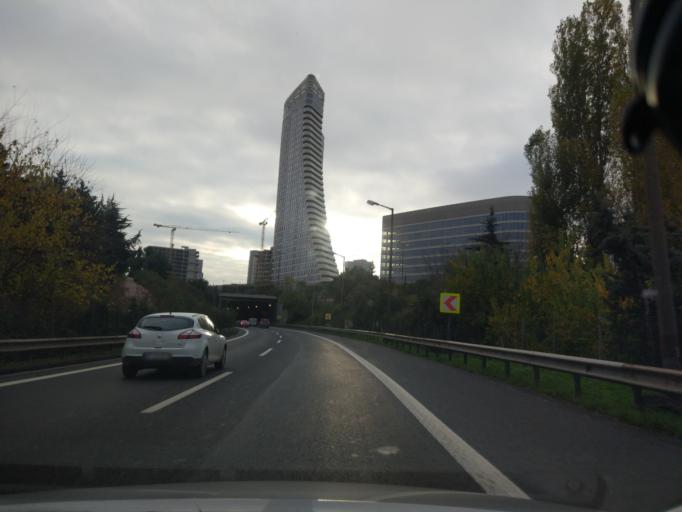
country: TR
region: Istanbul
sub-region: Atasehir
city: Atasehir
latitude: 40.9967
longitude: 29.1212
